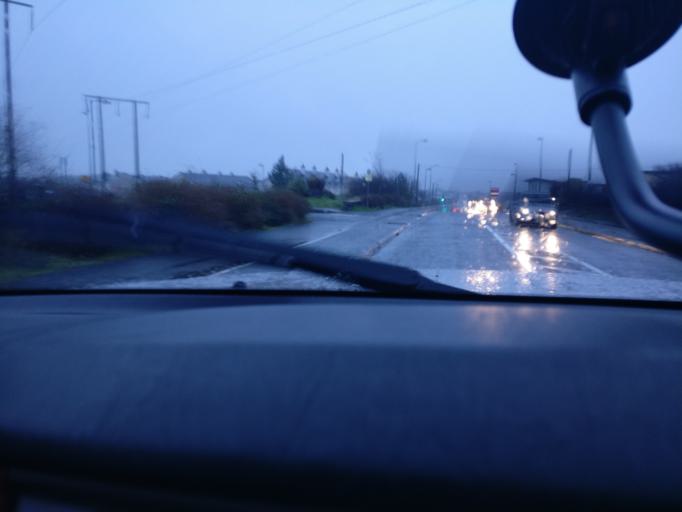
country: IE
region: Connaught
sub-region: County Galway
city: Gaillimh
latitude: 53.2889
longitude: -8.9864
